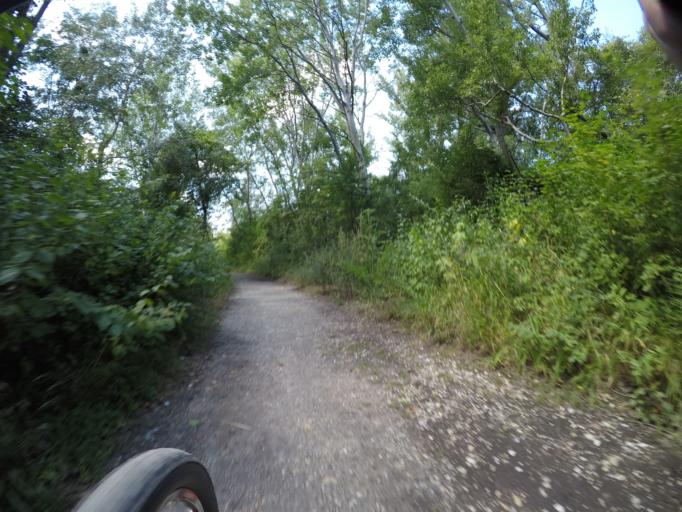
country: AT
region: Lower Austria
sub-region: Politischer Bezirk Wien-Umgebung
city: Schwechat
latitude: 48.1793
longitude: 16.4923
